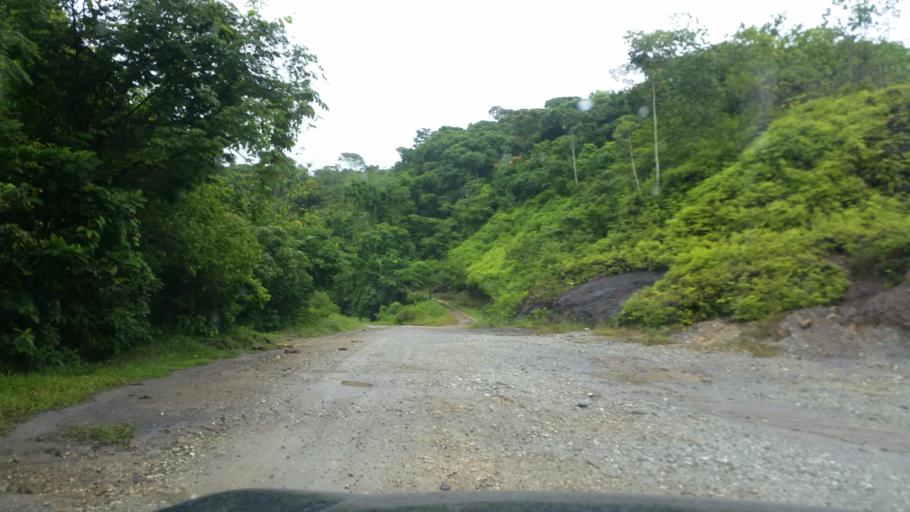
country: NI
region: Atlantico Norte (RAAN)
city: Bonanza
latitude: 14.0608
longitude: -84.6201
